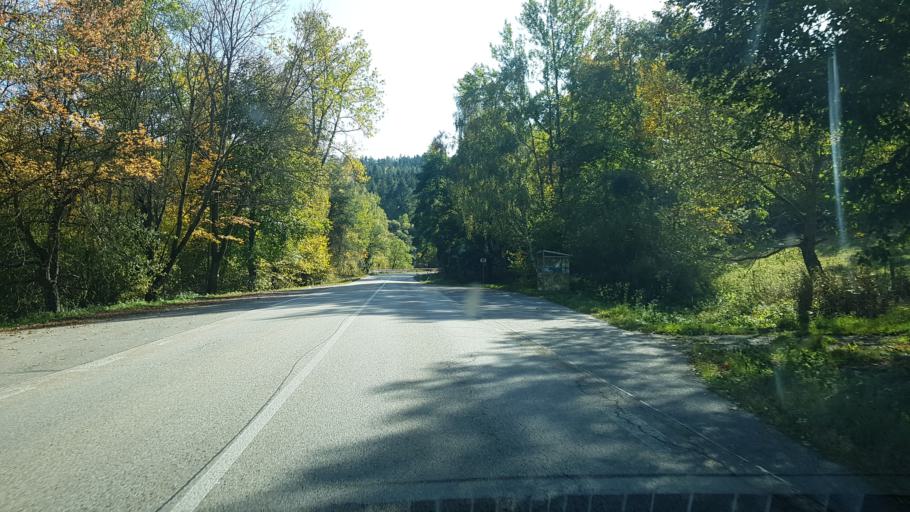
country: CZ
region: Jihocesky
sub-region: Okres Prachatice
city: Vimperk
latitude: 49.0846
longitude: 13.7865
